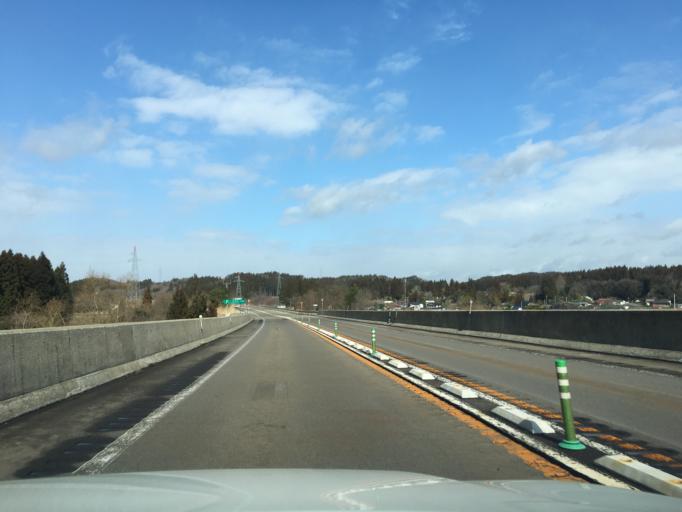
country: JP
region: Akita
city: Akita
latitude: 39.7358
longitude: 140.1747
